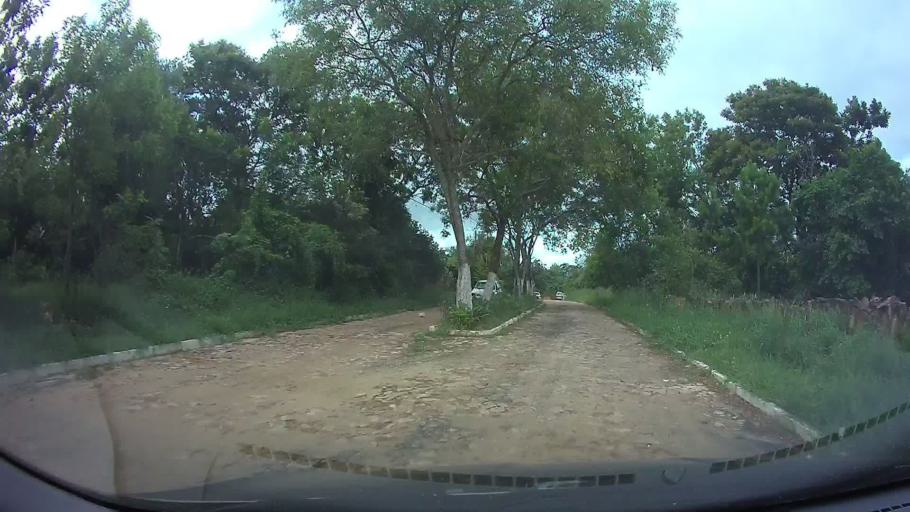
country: PY
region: Central
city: San Lorenzo
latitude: -25.2805
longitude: -57.4865
